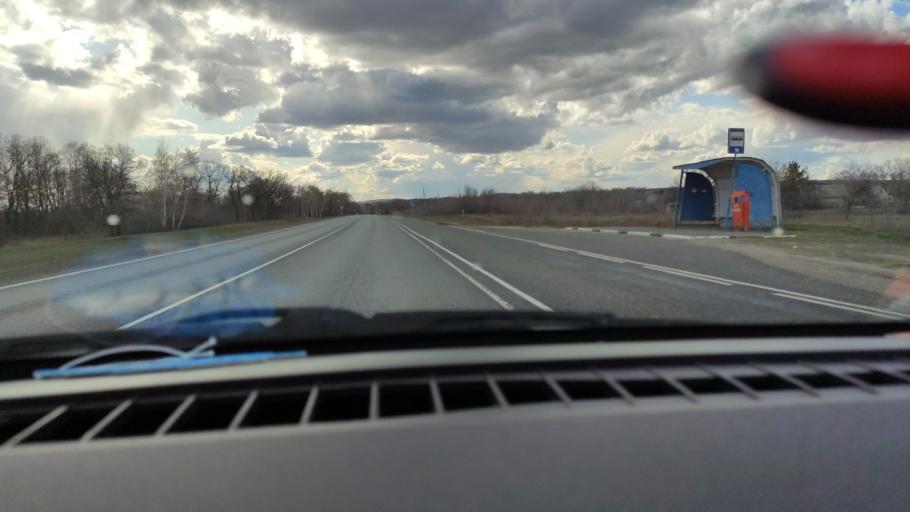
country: RU
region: Saratov
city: Tersa
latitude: 52.0855
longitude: 47.5995
